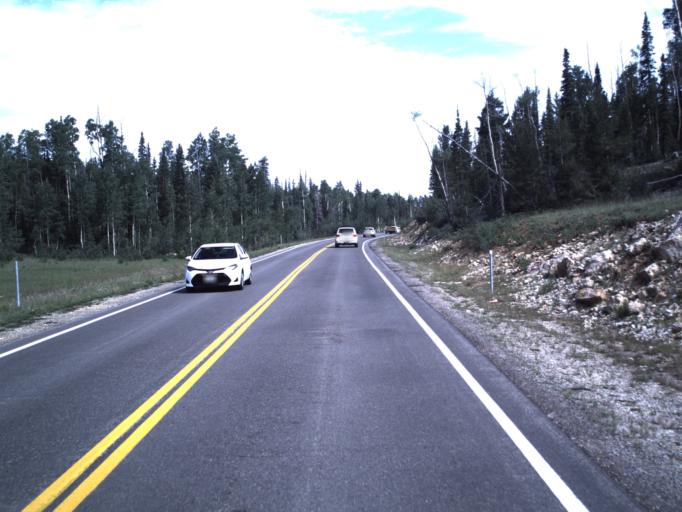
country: US
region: Utah
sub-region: Iron County
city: Parowan
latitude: 37.5445
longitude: -112.7853
